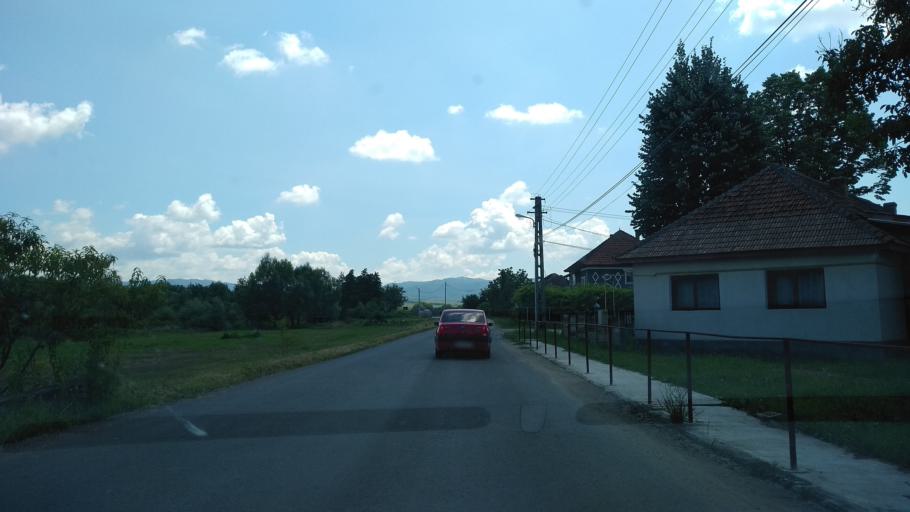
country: RO
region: Hunedoara
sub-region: Comuna Calan
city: Calan
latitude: 45.7186
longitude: 23.0350
